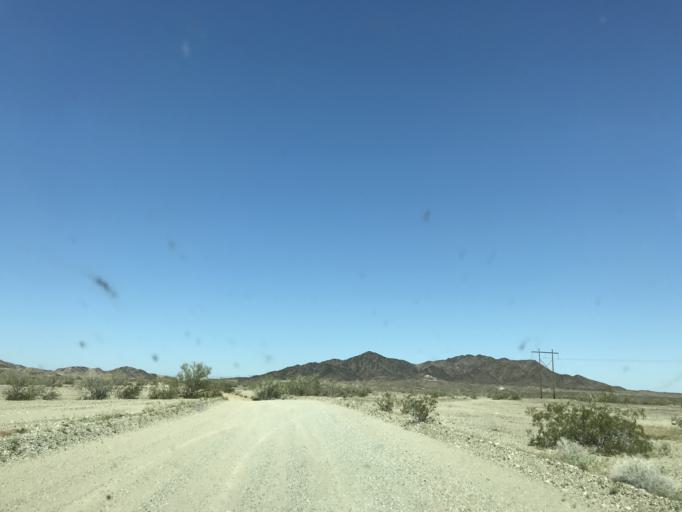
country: US
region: California
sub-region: Riverside County
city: Mesa Verde
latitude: 33.4916
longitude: -114.8060
